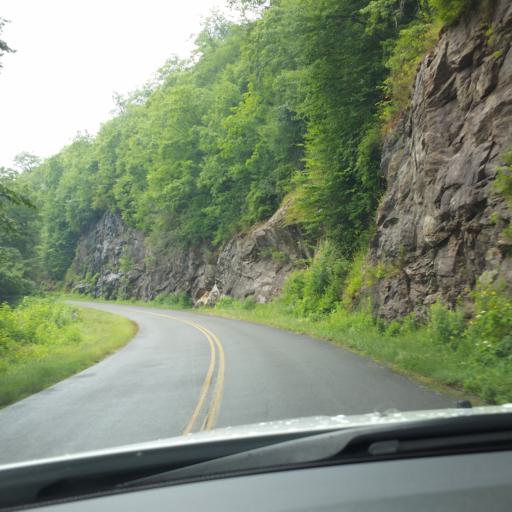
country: US
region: North Carolina
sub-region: Transylvania County
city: Brevard
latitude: 35.3193
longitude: -82.8307
